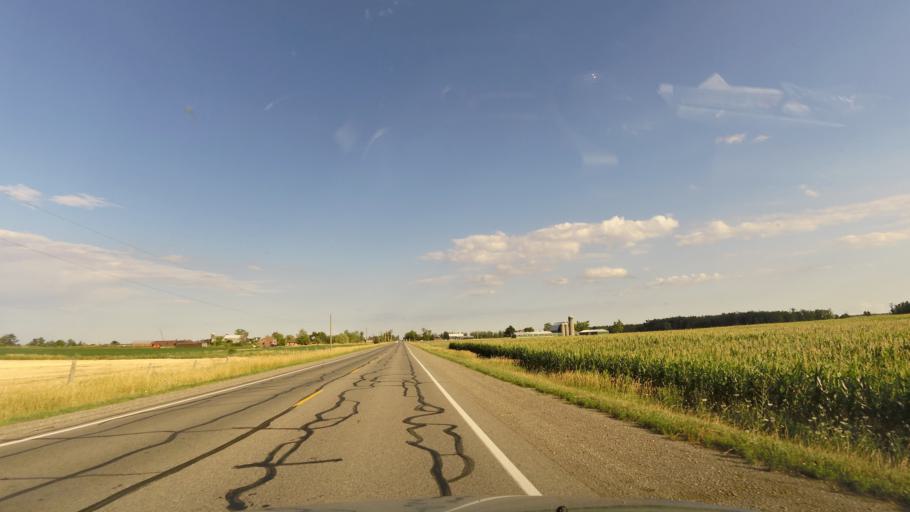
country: CA
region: Ontario
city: Brampton
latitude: 43.7072
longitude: -79.8843
